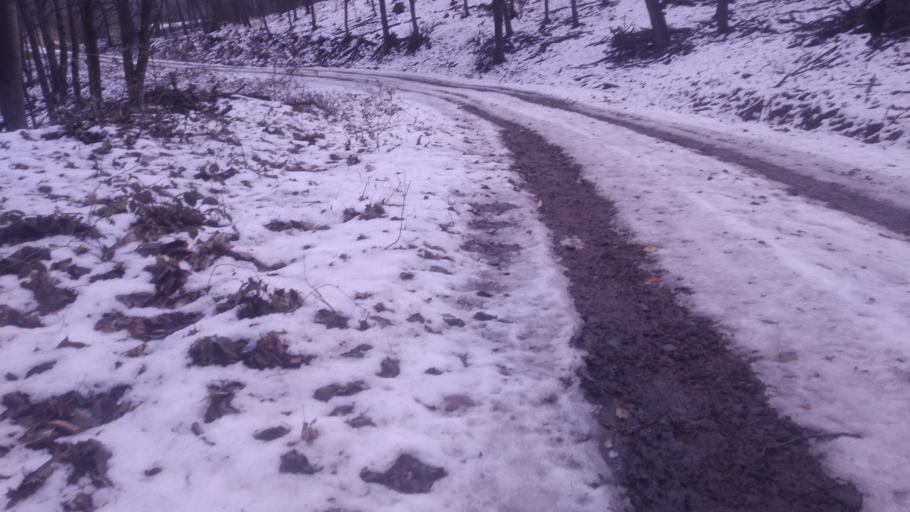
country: HU
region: Pest
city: Pilisszentkereszt
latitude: 47.7368
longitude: 18.9352
